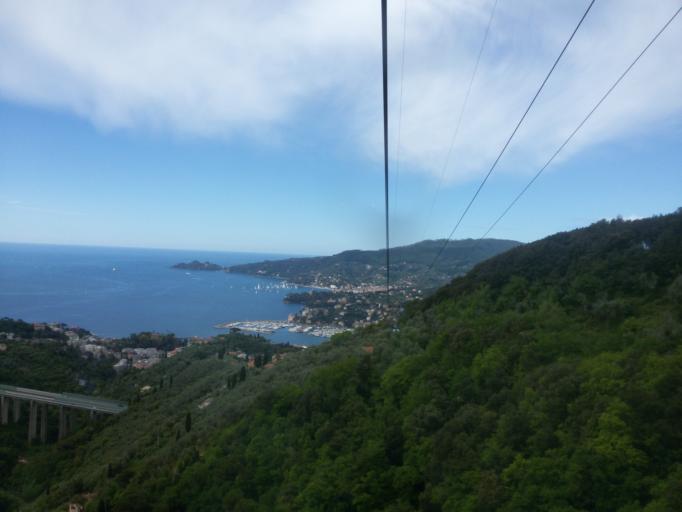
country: IT
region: Liguria
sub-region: Provincia di Genova
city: Rapallo
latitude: 44.3605
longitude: 9.2444
